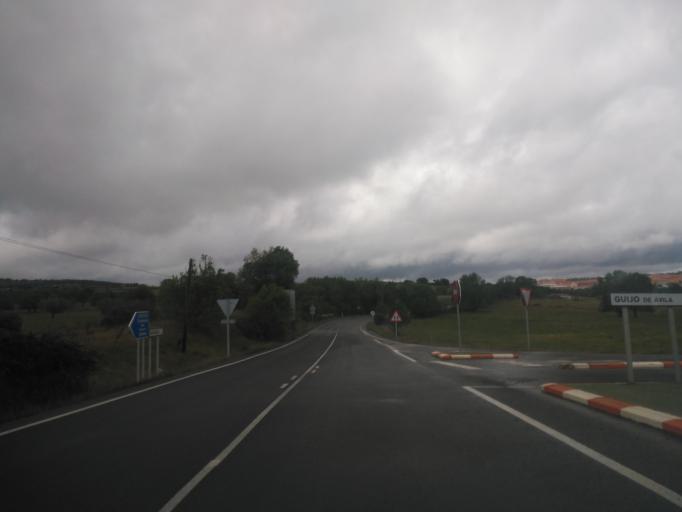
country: ES
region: Castille and Leon
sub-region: Provincia de Salamanca
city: Fuentes de Bejar
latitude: 40.5249
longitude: -5.6737
